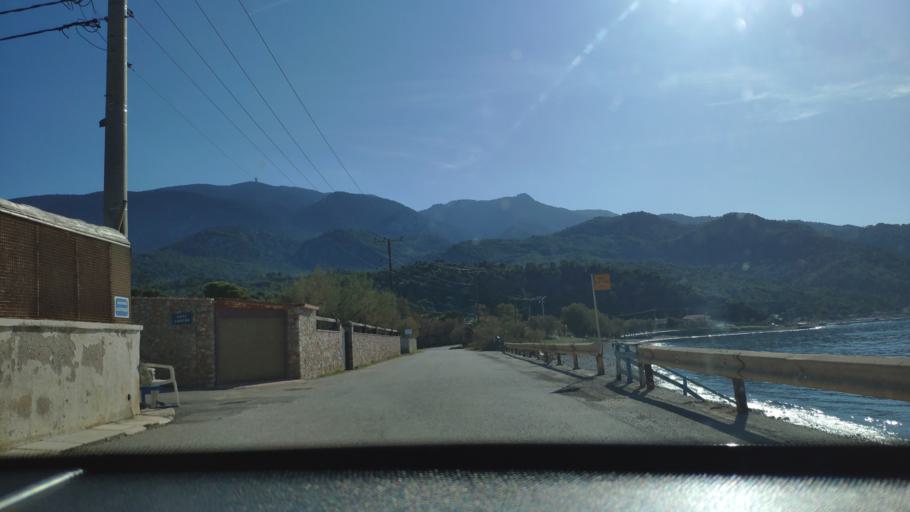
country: GR
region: Attica
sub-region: Nomarchia Dytikis Attikis
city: Kineta
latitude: 38.0696
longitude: 23.1505
